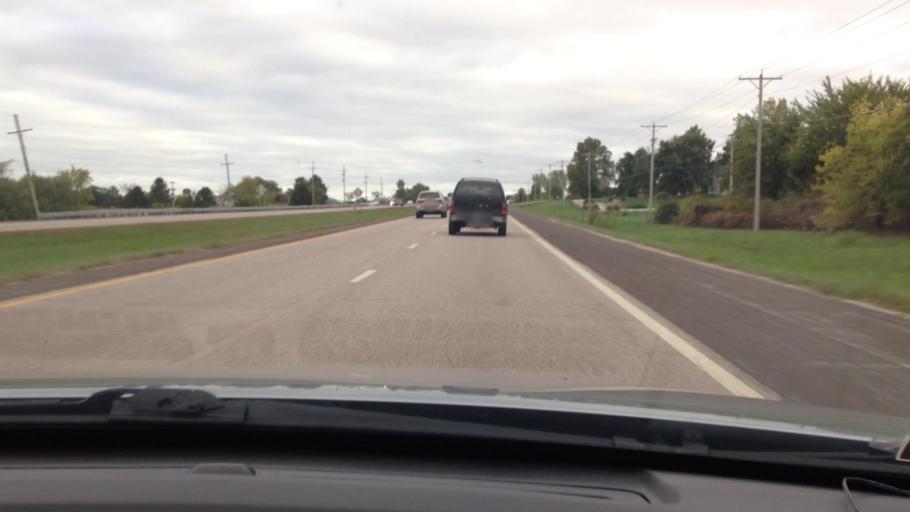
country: US
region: Kansas
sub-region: Leavenworth County
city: Basehor
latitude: 39.1844
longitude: -94.9006
